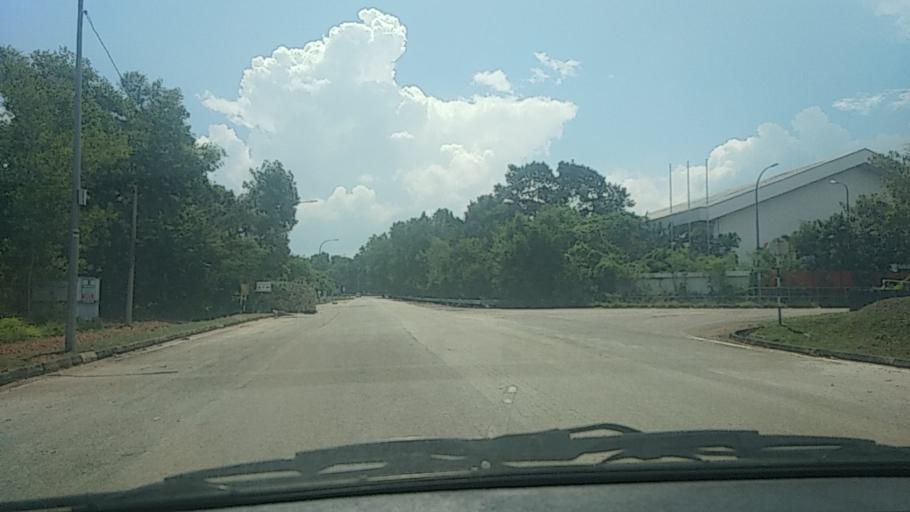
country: MY
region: Kedah
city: Sungai Petani
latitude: 5.6643
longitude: 100.5315
